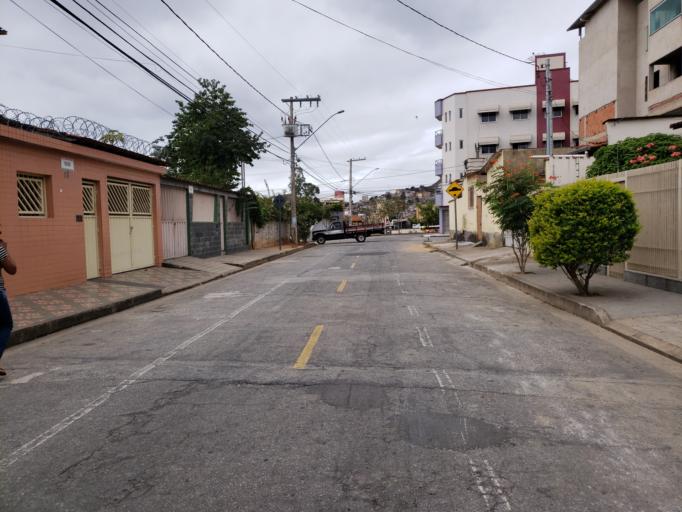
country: BR
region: Minas Gerais
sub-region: Ipatinga
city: Ipatinga
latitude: -19.4580
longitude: -42.5621
